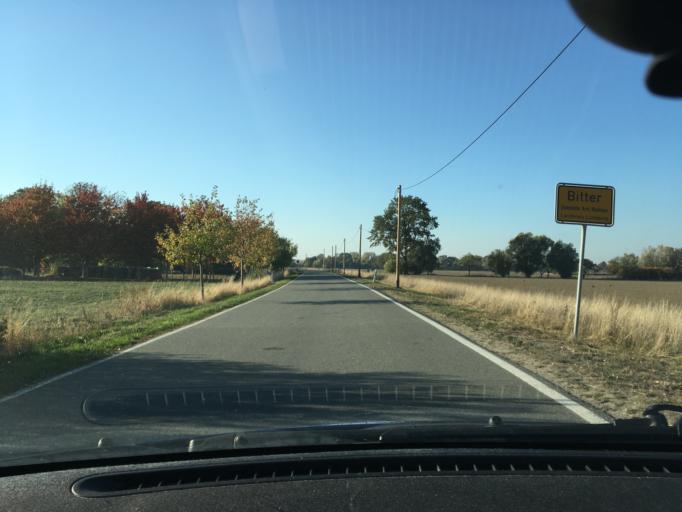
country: DE
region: Lower Saxony
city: Hitzacker
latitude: 53.1652
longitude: 11.0467
